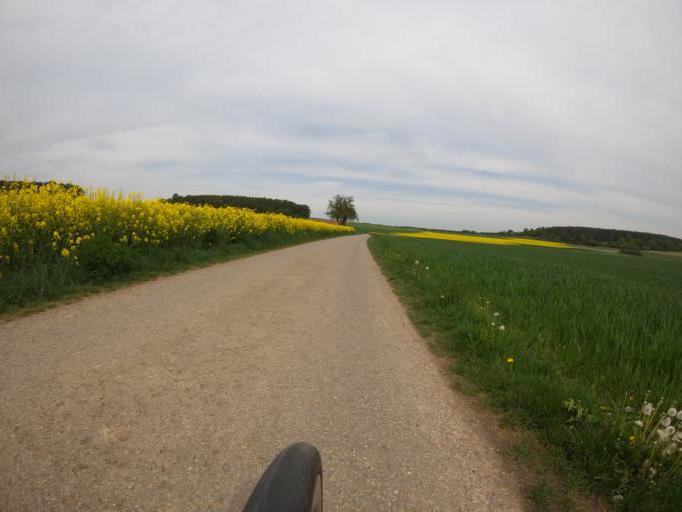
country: DE
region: Baden-Wuerttemberg
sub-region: Regierungsbezirk Stuttgart
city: Aidlingen
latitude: 48.6924
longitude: 8.8680
